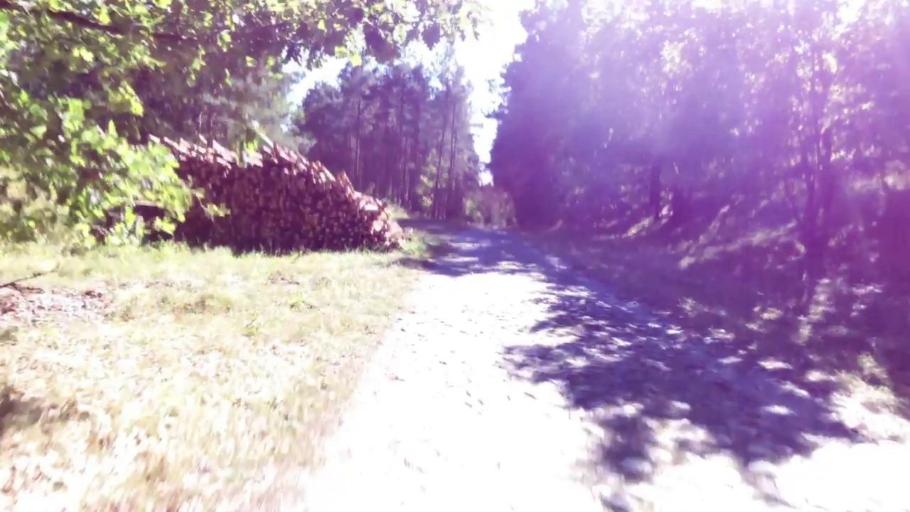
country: PL
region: West Pomeranian Voivodeship
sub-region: Powiat szczecinecki
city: Szczecinek
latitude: 53.7959
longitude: 16.6875
